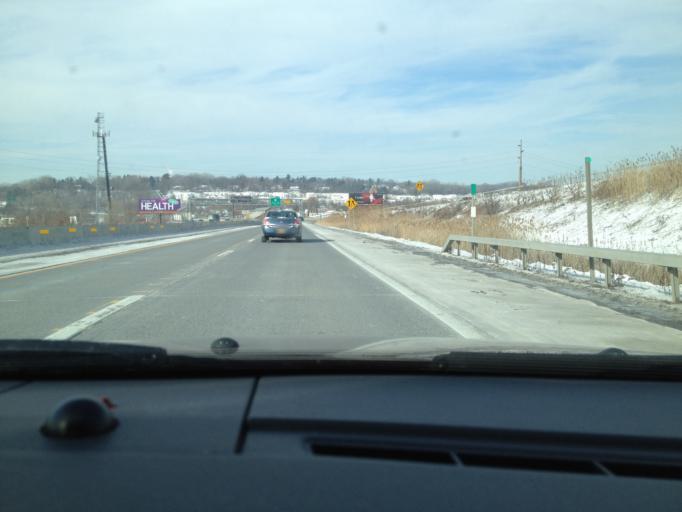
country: US
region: New York
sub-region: Albany County
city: Menands
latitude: 42.6679
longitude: -73.7339
